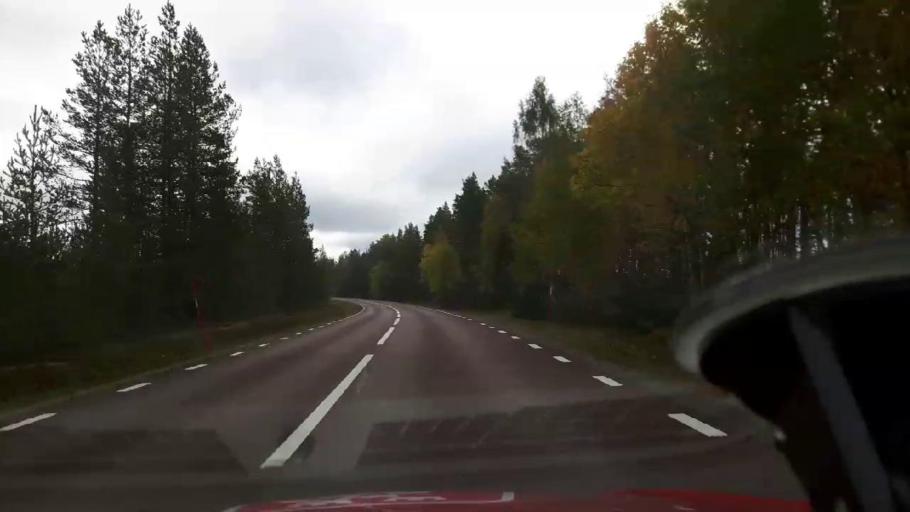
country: SE
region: Jaemtland
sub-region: Harjedalens Kommun
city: Sveg
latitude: 62.1812
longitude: 14.8800
